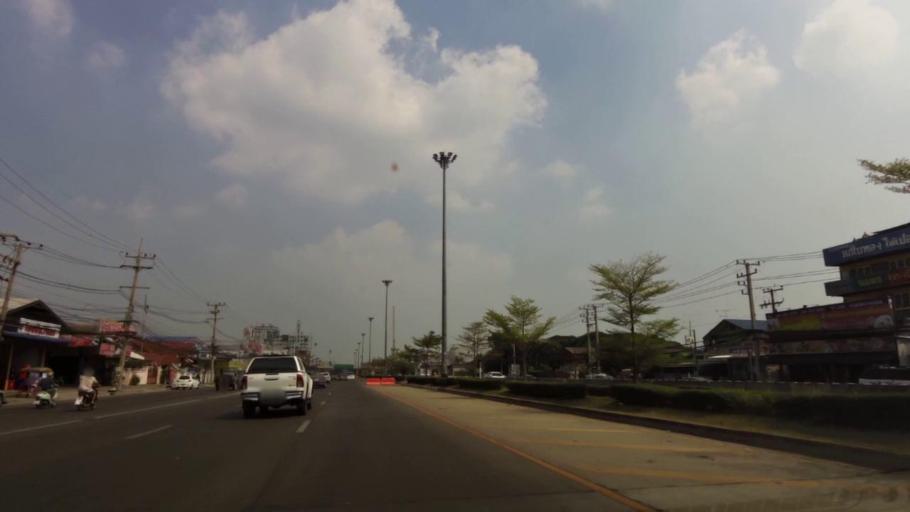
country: TH
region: Phra Nakhon Si Ayutthaya
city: Phra Nakhon Si Ayutthaya
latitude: 14.3540
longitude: 100.5926
